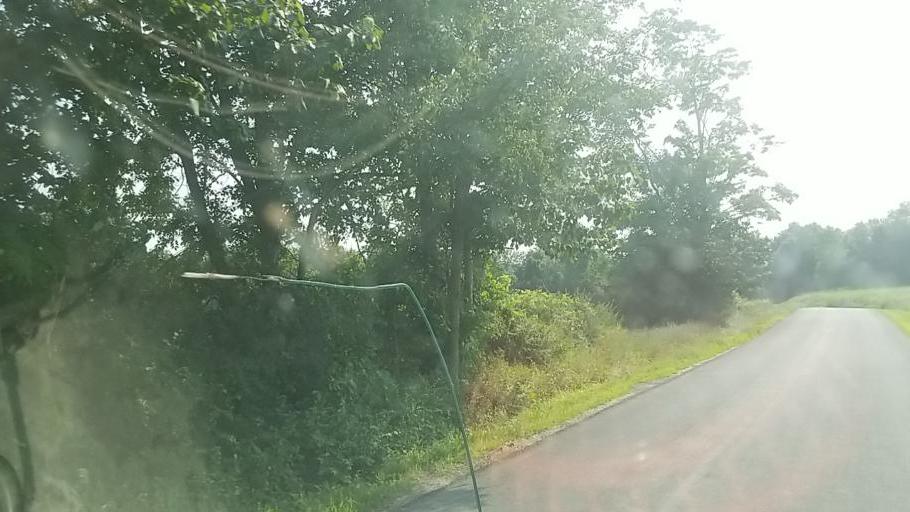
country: US
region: New York
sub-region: Montgomery County
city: Fonda
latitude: 42.9156
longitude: -74.3469
